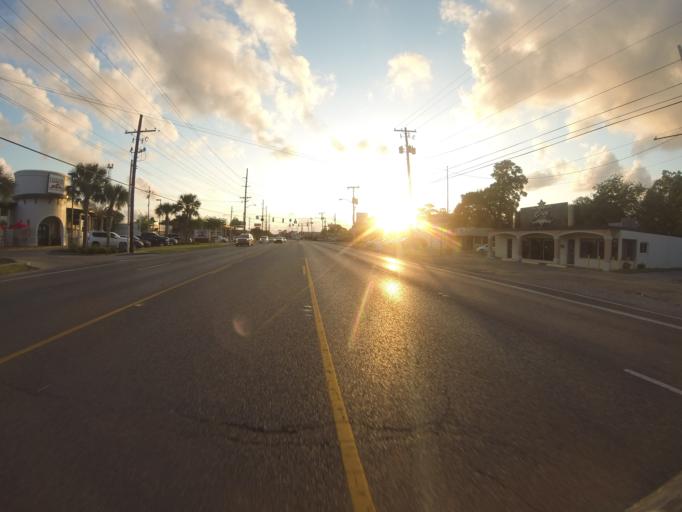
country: US
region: Louisiana
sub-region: Lafayette Parish
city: Lafayette
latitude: 30.2038
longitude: -92.0475
